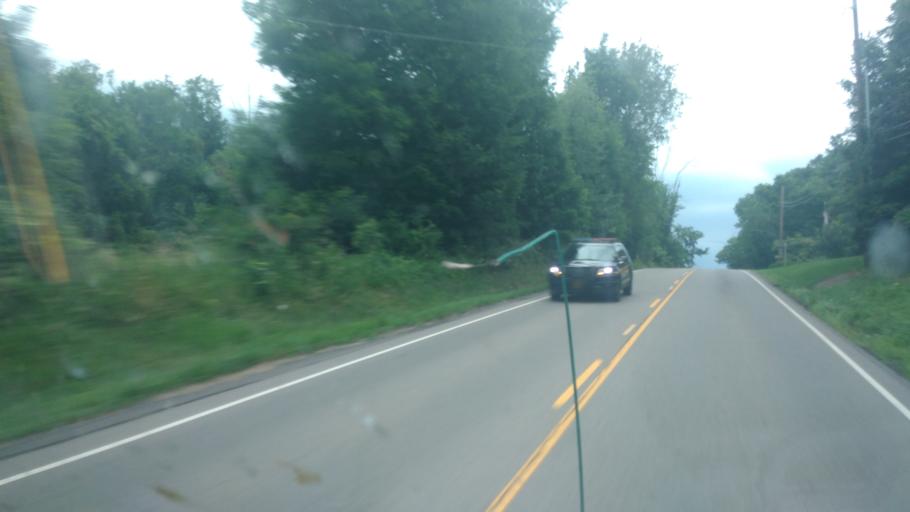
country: US
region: Ohio
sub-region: Licking County
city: Granville
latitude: 40.0918
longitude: -82.5202
